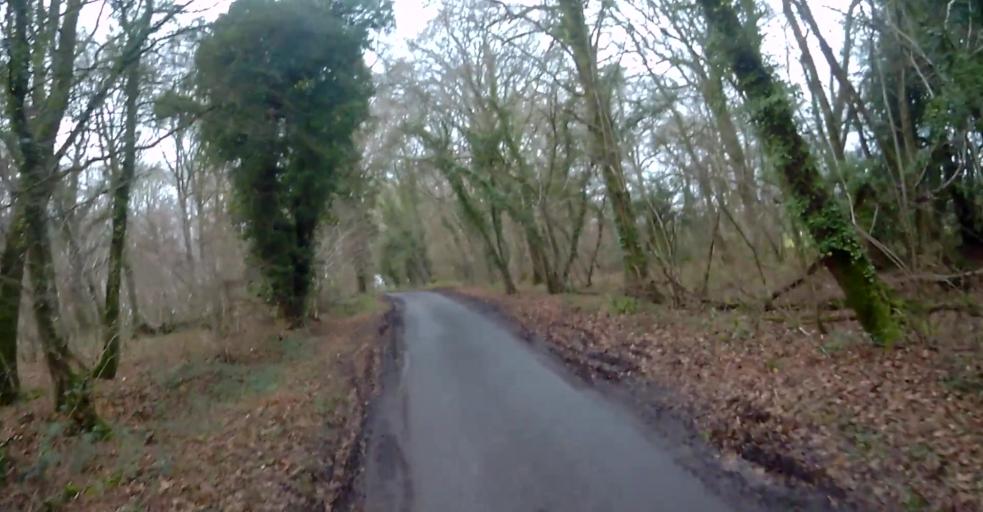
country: GB
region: England
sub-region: Hampshire
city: Overton
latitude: 51.2305
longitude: -1.2440
